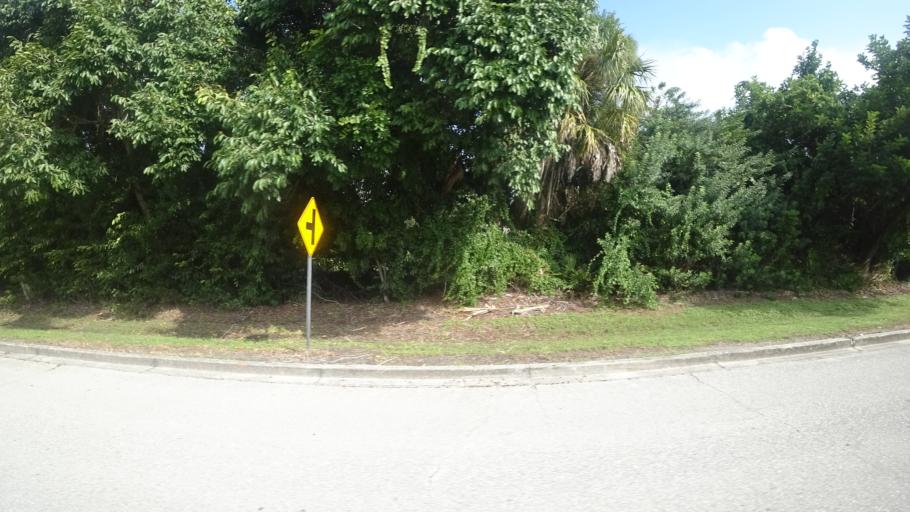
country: US
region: Florida
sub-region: Manatee County
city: South Bradenton
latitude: 27.4565
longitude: -82.6042
